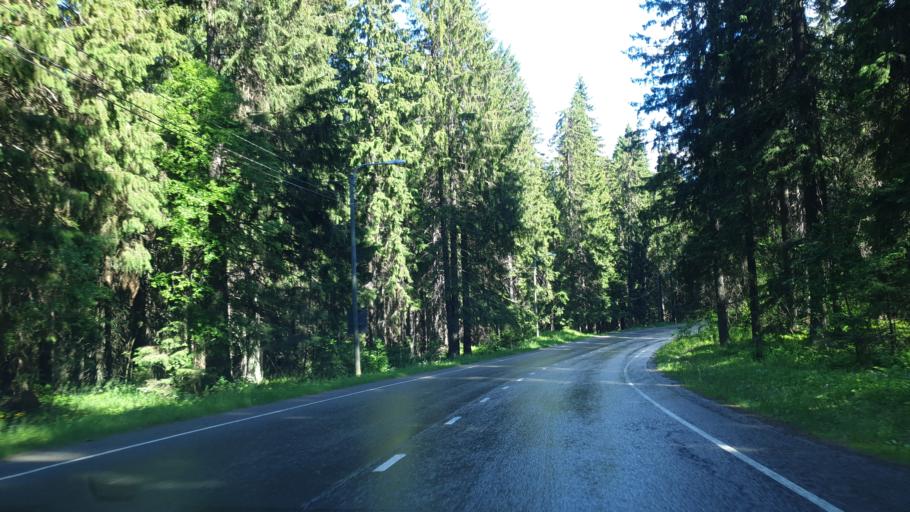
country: FI
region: Northern Savo
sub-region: Kuopio
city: Kuopio
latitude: 62.9083
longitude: 27.6674
